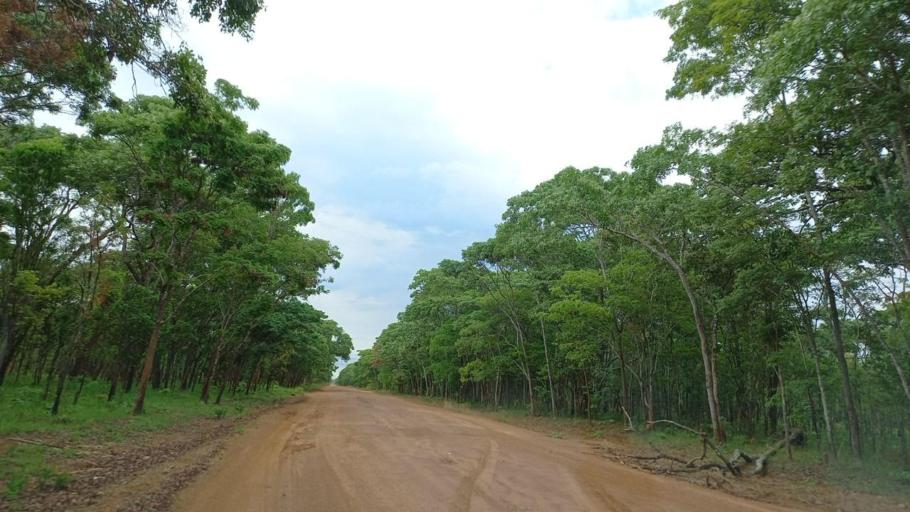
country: ZM
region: North-Western
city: Kalengwa
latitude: -13.3625
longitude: 25.0755
